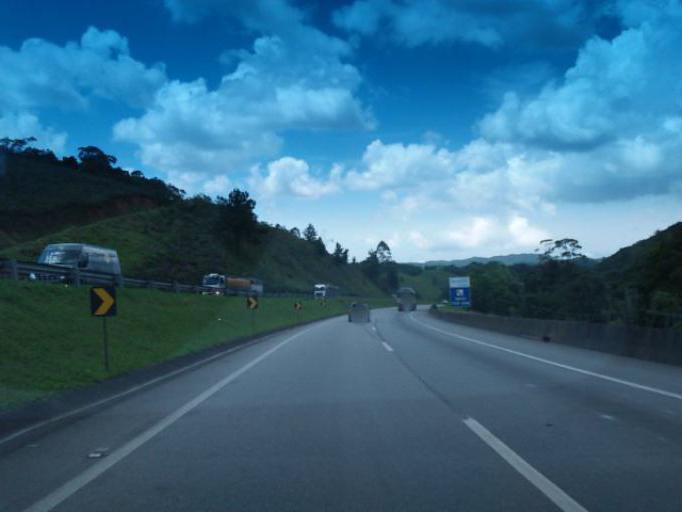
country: BR
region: Sao Paulo
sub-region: Juquitiba
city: Juquitiba
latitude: -23.9952
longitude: -47.1480
